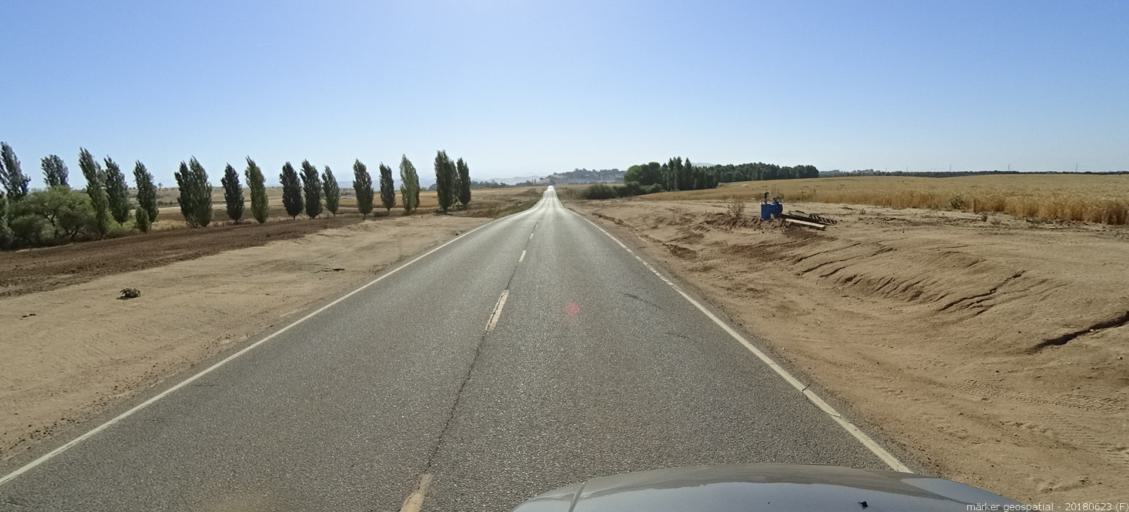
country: US
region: California
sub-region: Madera County
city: Bonadelle Ranchos-Madera Ranchos
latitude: 36.9596
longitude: -119.7781
